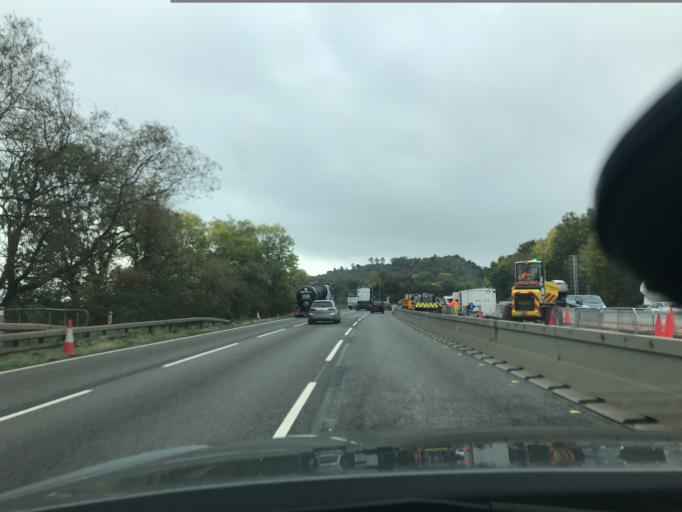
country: GB
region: England
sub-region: Staffordshire
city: Newcastle under Lyme
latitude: 52.9692
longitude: -2.2234
